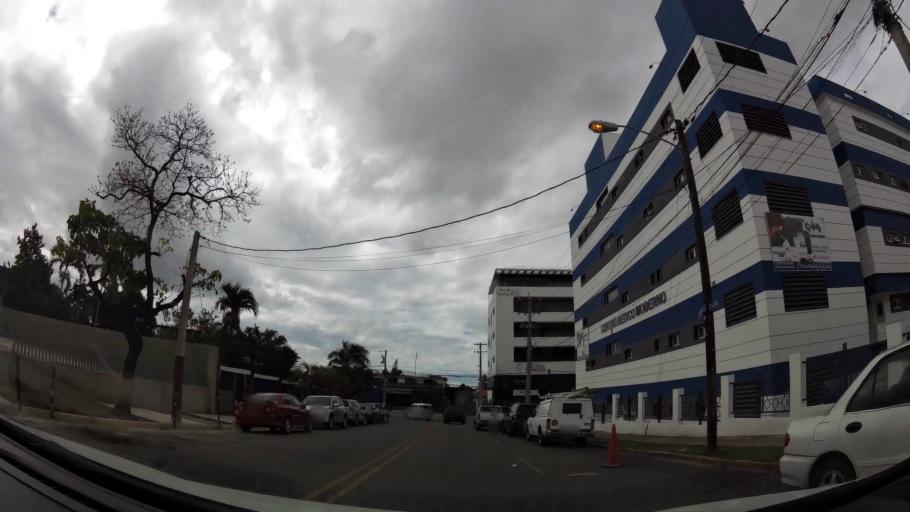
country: DO
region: Nacional
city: Bella Vista
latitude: 18.4762
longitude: -69.9573
